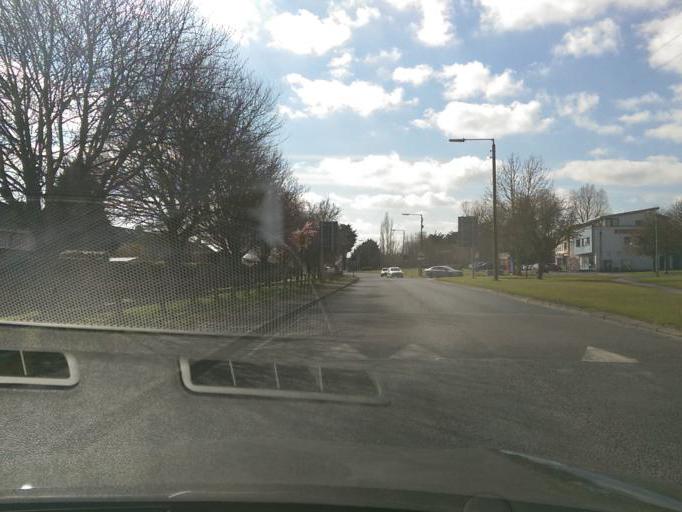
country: IE
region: Leinster
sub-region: Kildare
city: Leixlip
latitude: 53.3624
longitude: -6.5002
